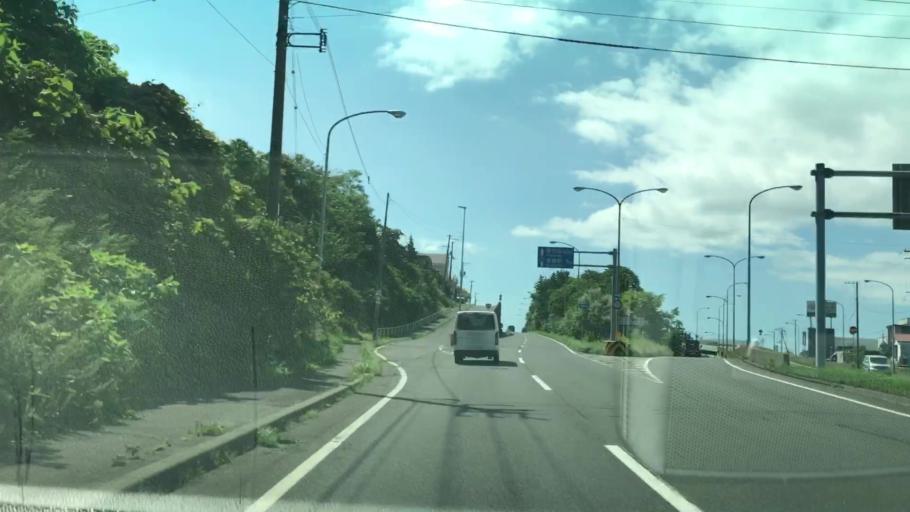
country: JP
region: Hokkaido
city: Muroran
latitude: 42.3541
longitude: 141.0475
